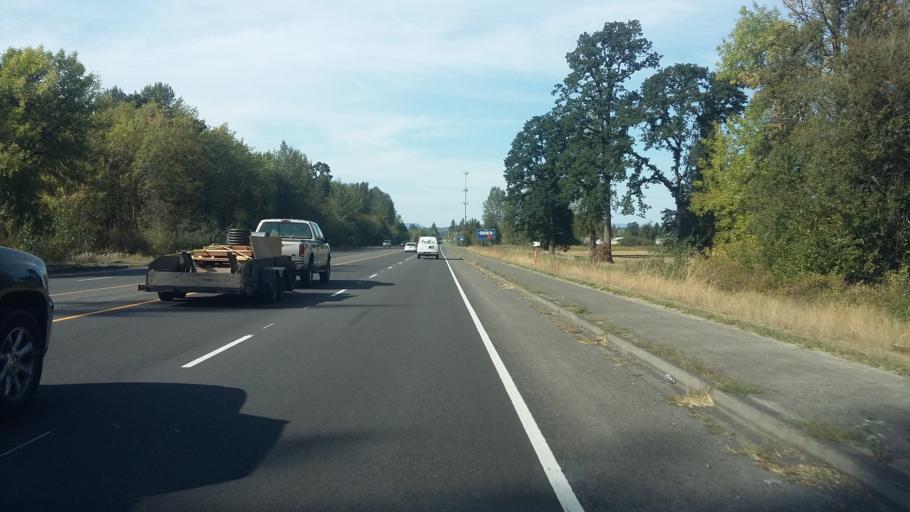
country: US
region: Washington
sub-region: Clark County
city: Battle Ground
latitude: 45.7731
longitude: -122.5474
